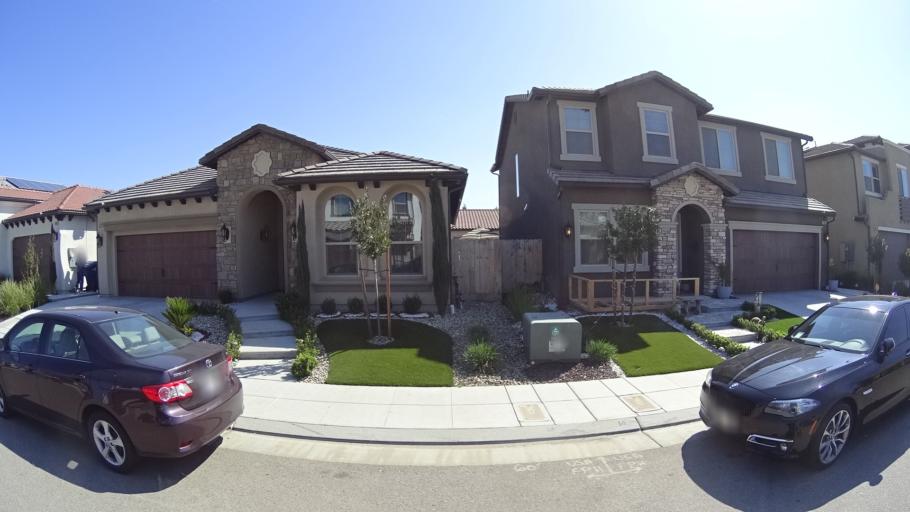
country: US
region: California
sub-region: Fresno County
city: Clovis
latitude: 36.9079
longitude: -119.7485
